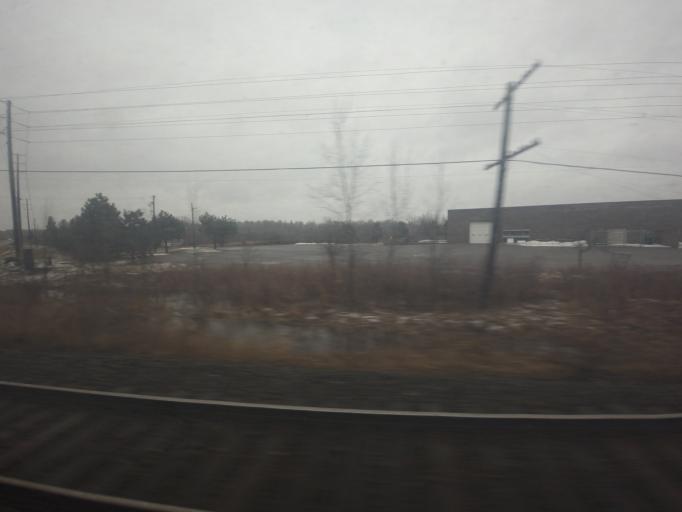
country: CA
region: Ontario
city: Kingston
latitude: 44.2984
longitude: -76.4208
